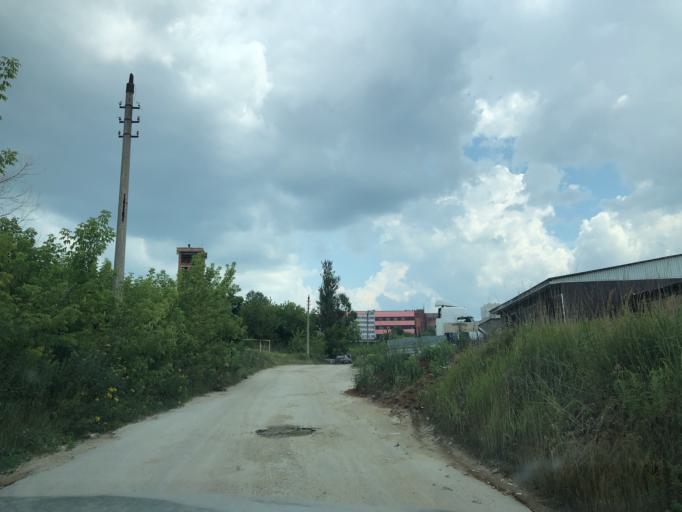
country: RU
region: Tula
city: Mendeleyevskiy
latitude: 54.1604
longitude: 37.5753
